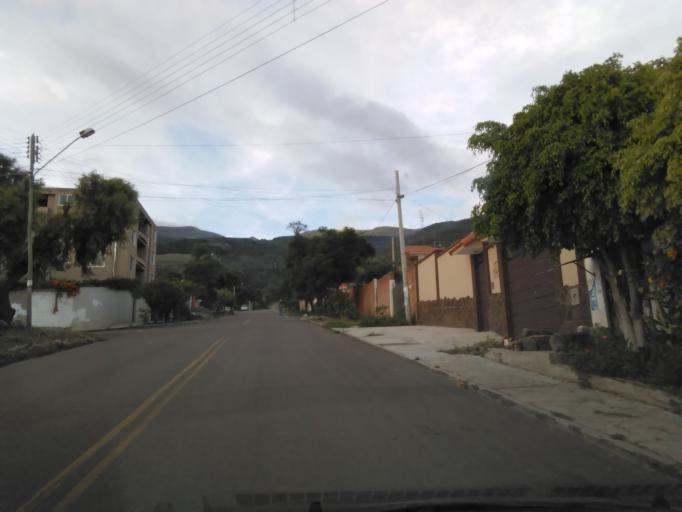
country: BO
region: Cochabamba
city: Cochabamba
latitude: -17.3551
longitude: -66.1551
